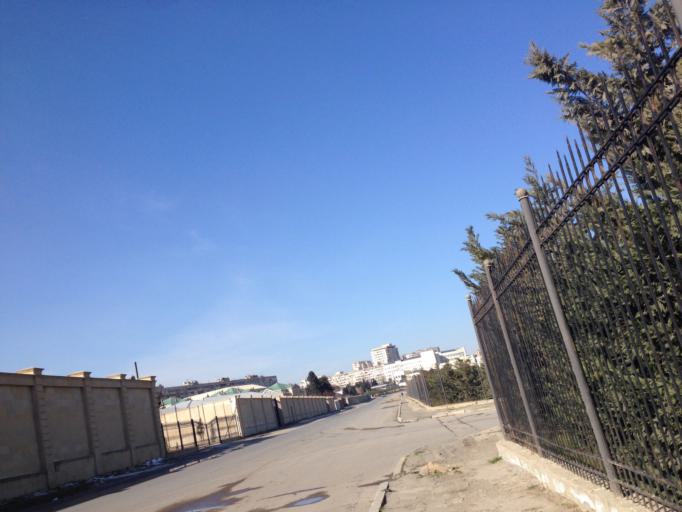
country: AZ
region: Baki
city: Baku
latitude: 40.4088
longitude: 49.8563
